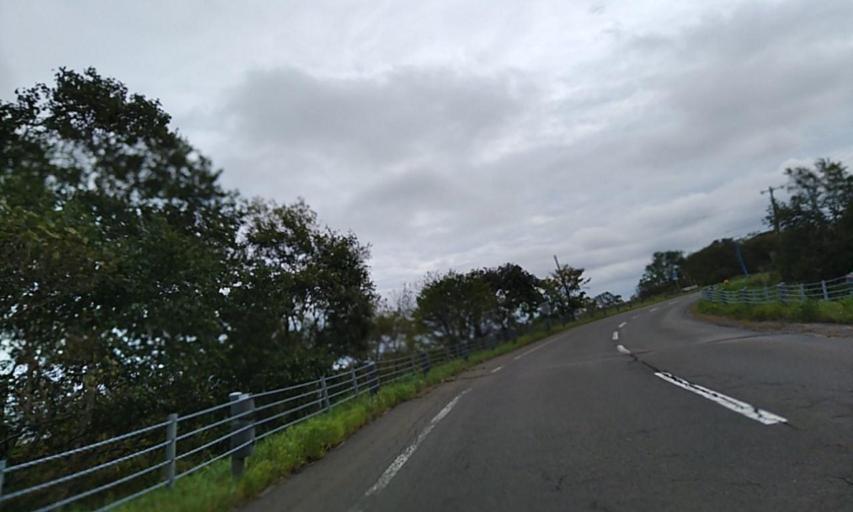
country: JP
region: Hokkaido
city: Shibetsu
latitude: 43.5206
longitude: 145.2419
